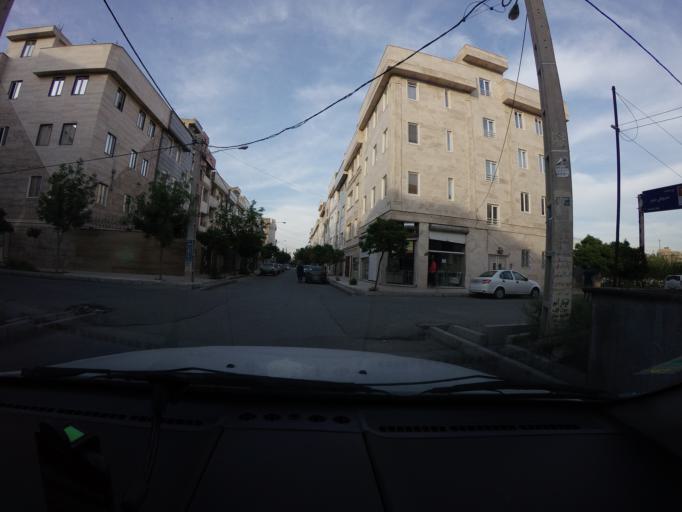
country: IR
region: Tehran
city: Eslamshahr
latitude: 35.5331
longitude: 51.2151
